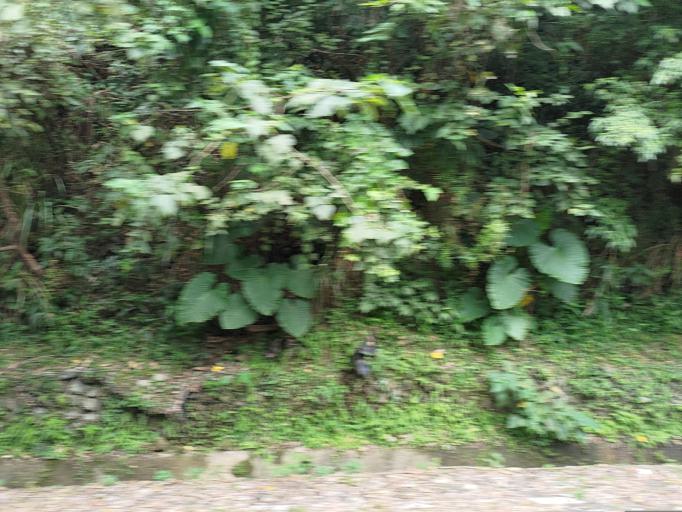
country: TW
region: Taiwan
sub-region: Miaoli
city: Miaoli
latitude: 24.6005
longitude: 121.0289
